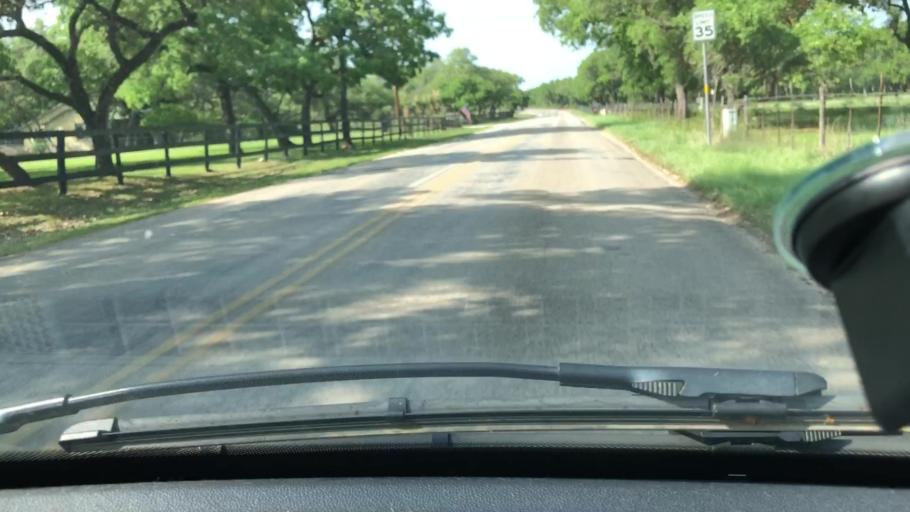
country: US
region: Texas
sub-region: Comal County
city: Bulverde
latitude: 29.7618
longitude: -98.4586
